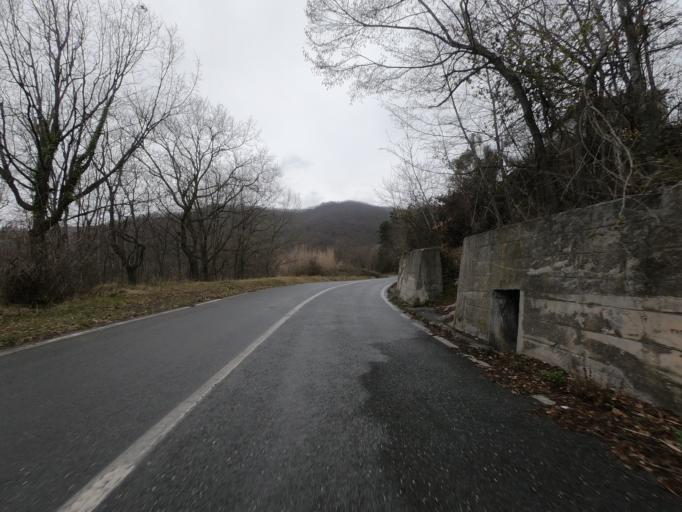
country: IT
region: Liguria
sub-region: Provincia di Imperia
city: Cesio
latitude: 44.0223
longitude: 7.9886
